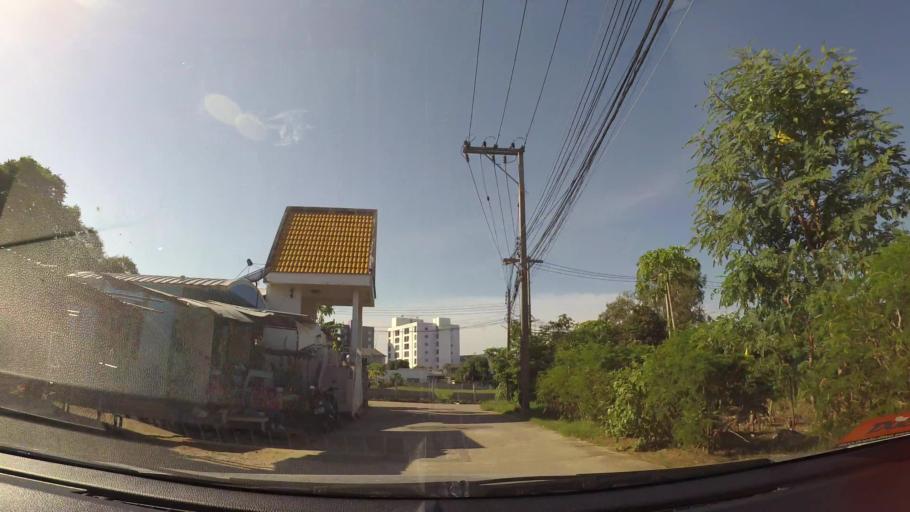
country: TH
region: Chon Buri
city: Si Racha
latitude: 13.1552
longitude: 100.9314
